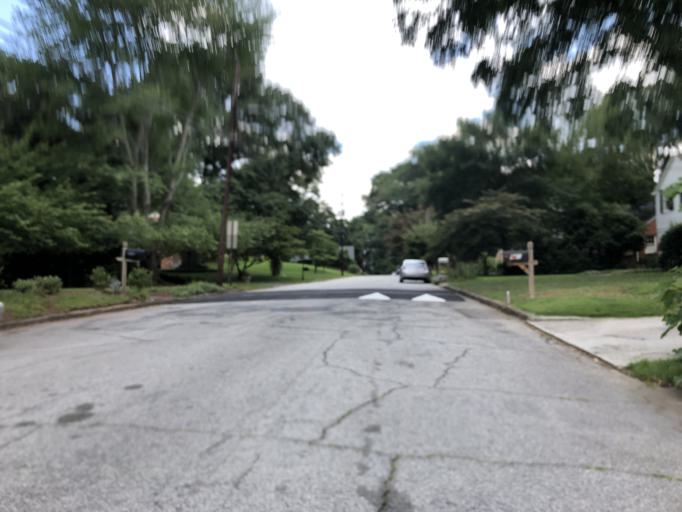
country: US
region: Georgia
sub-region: DeKalb County
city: North Decatur
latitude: 33.7824
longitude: -84.3038
